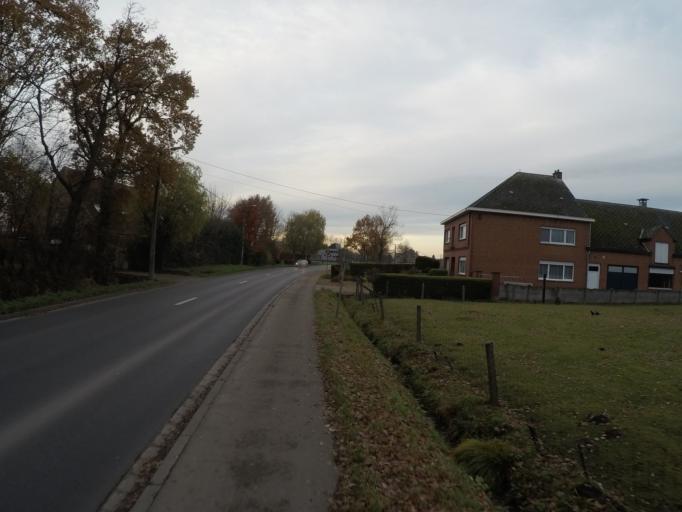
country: BE
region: Flanders
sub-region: Provincie Antwerpen
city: Berlaar
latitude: 51.1097
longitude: 4.6740
